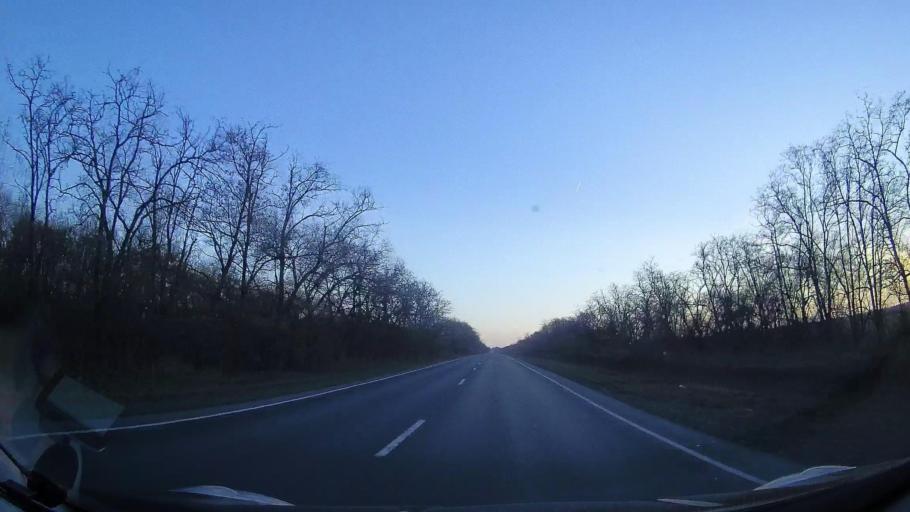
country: RU
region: Rostov
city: Bagayevskaya
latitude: 47.1274
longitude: 40.2766
